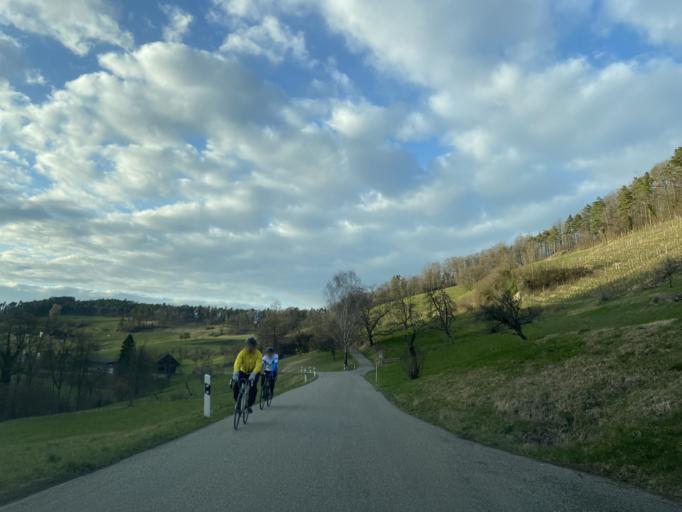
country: CH
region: Zurich
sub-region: Bezirk Winterthur
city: Wuelflingen (Kreis 6) / Niederfeld
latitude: 47.5048
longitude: 8.6602
